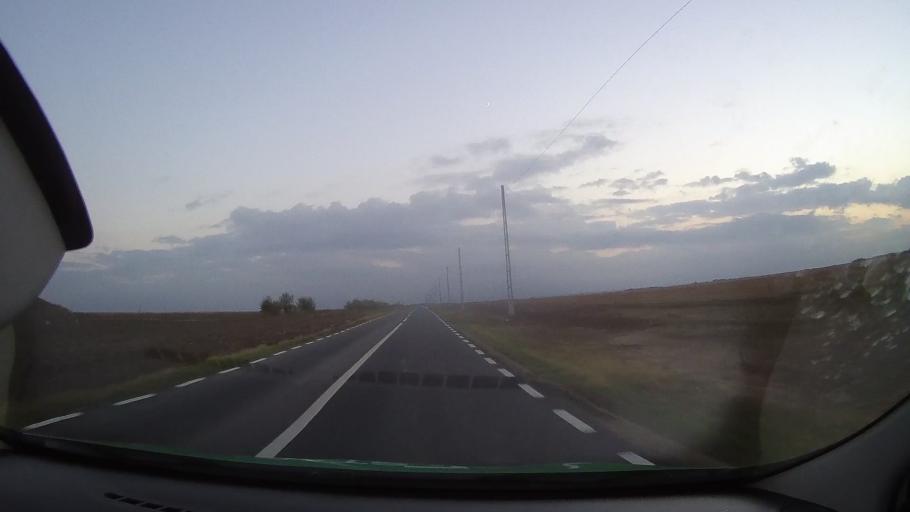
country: RO
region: Constanta
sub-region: Comuna Oltina
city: Oltina
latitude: 44.1318
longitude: 27.6686
